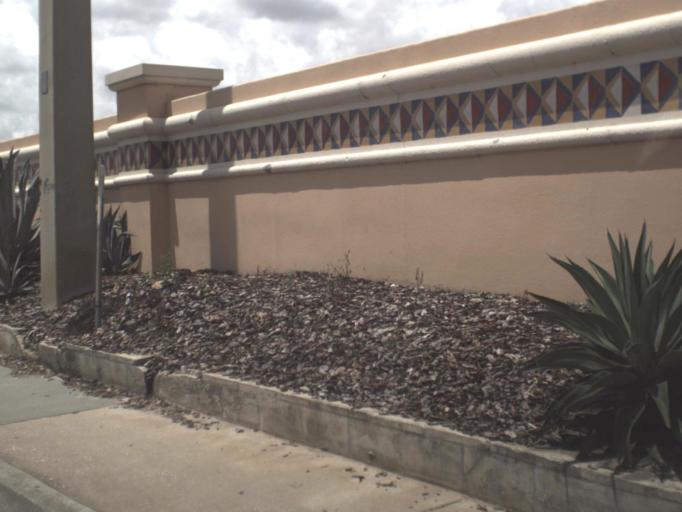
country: US
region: Florida
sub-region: Hillsborough County
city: Temple Terrace
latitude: 28.0327
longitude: -82.4175
